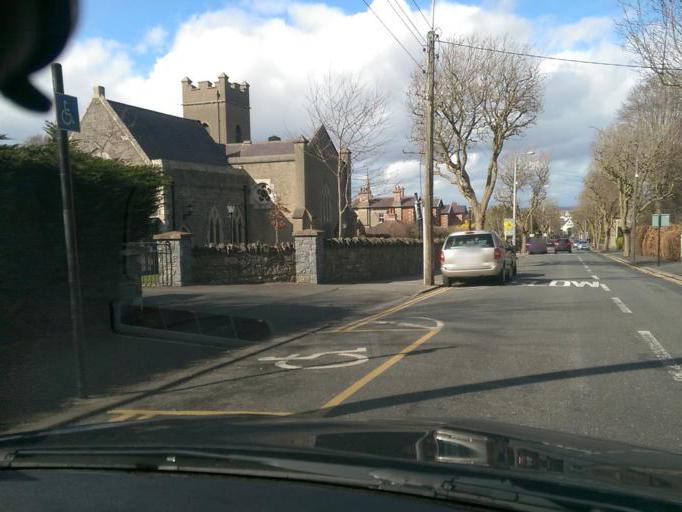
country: IE
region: Leinster
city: Malahide
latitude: 53.4479
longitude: -6.1530
